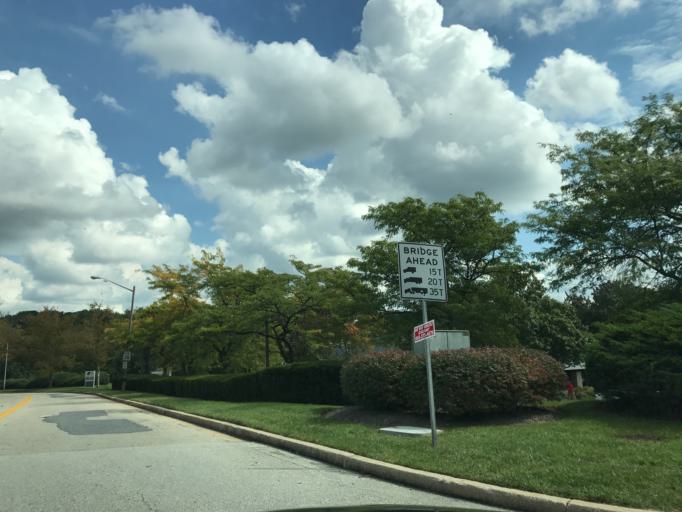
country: US
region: Maryland
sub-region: Baltimore County
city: Woodlawn
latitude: 39.3276
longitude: -76.7476
